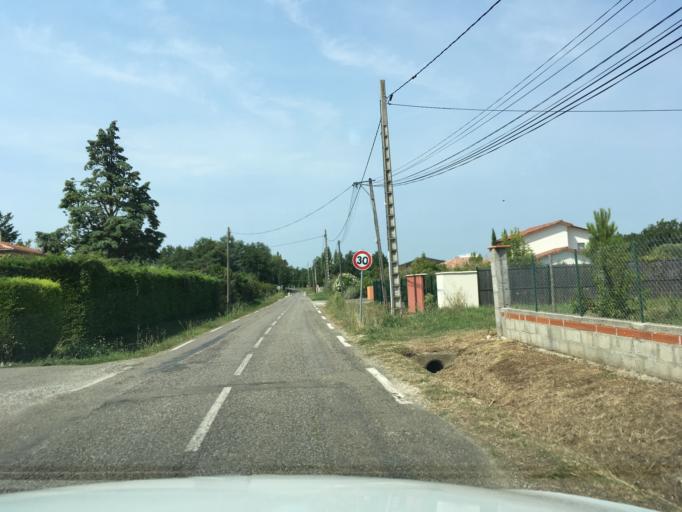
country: FR
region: Midi-Pyrenees
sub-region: Departement du Tarn-et-Garonne
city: Corbarieu
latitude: 43.9686
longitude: 1.3735
